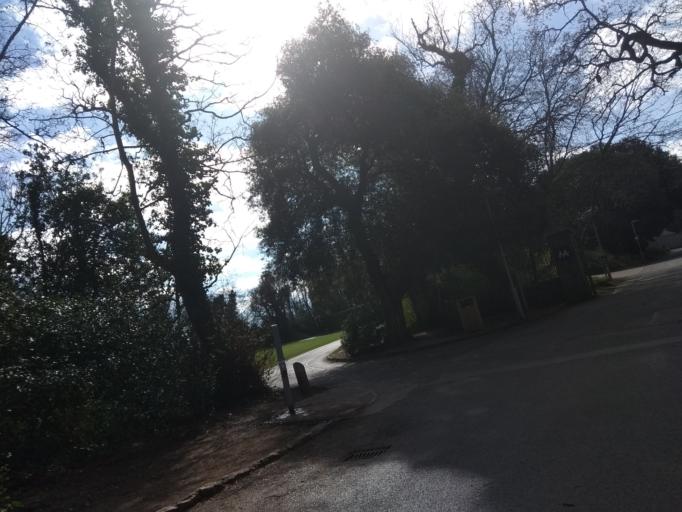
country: IE
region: Leinster
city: Malahide
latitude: 53.4472
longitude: -6.1588
